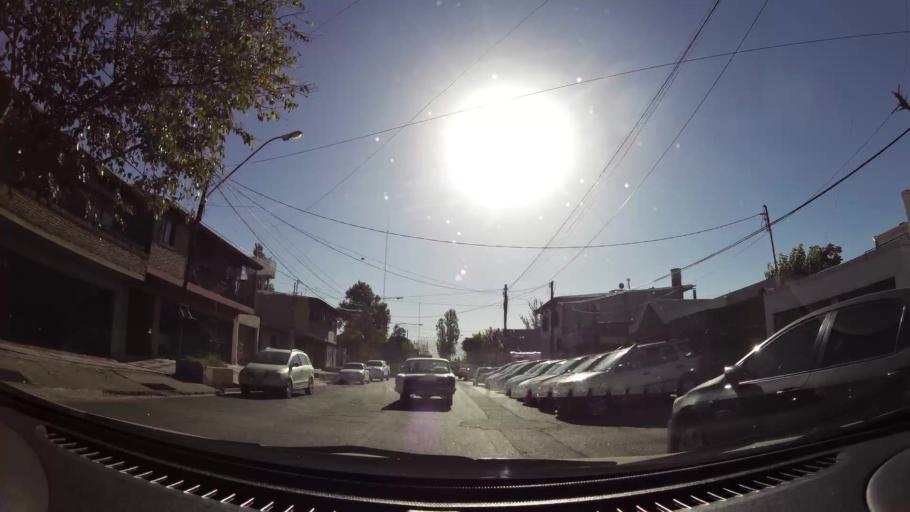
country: AR
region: Mendoza
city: Villa Nueva
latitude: -32.9032
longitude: -68.8042
